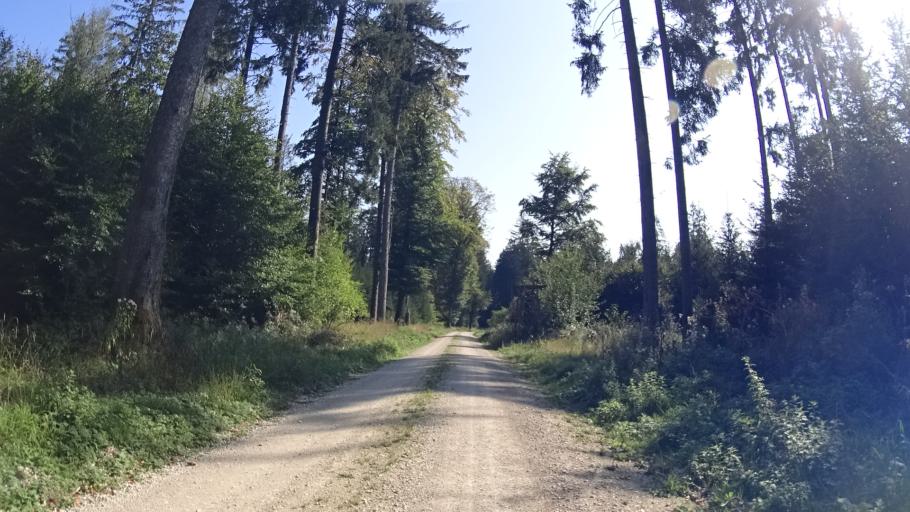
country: DE
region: Bavaria
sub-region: Upper Bavaria
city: Pollenfeld
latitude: 48.9464
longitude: 11.2536
